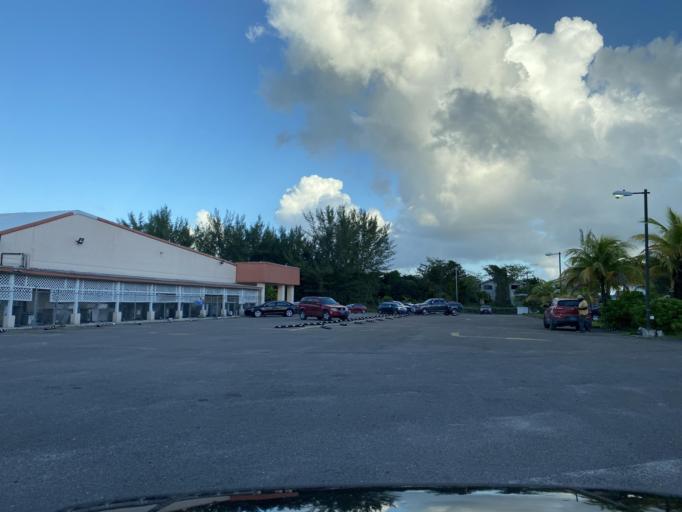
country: BS
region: New Providence
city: Nassau
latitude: 25.0740
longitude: -77.4239
